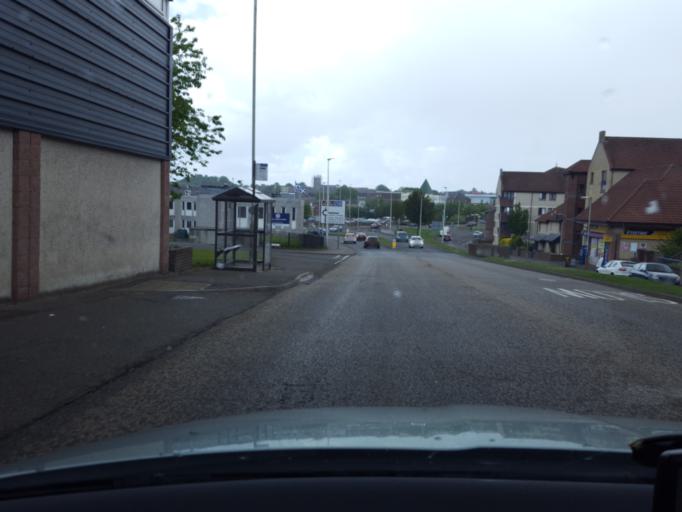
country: GB
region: Scotland
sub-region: Angus
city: Arbroath
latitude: 56.5640
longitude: -2.5842
